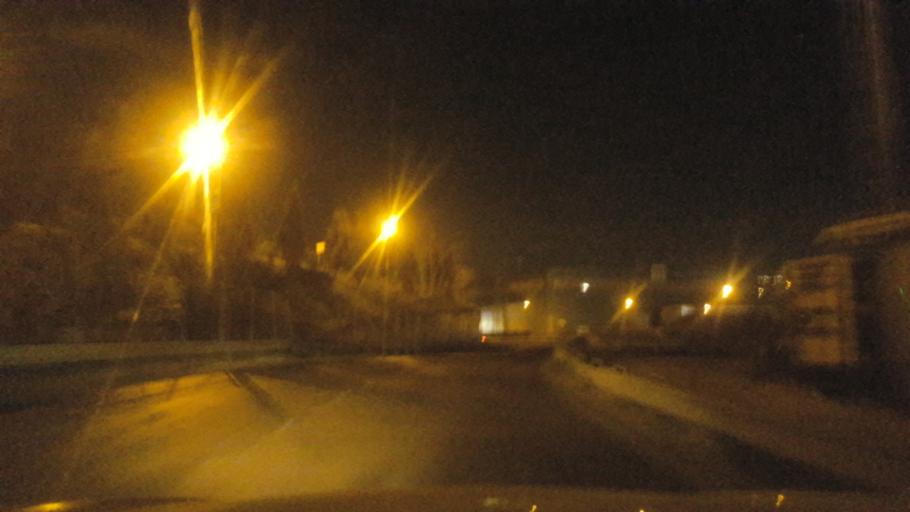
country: TR
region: Kocaeli
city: Tavsancil
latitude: 40.7782
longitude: 29.5299
